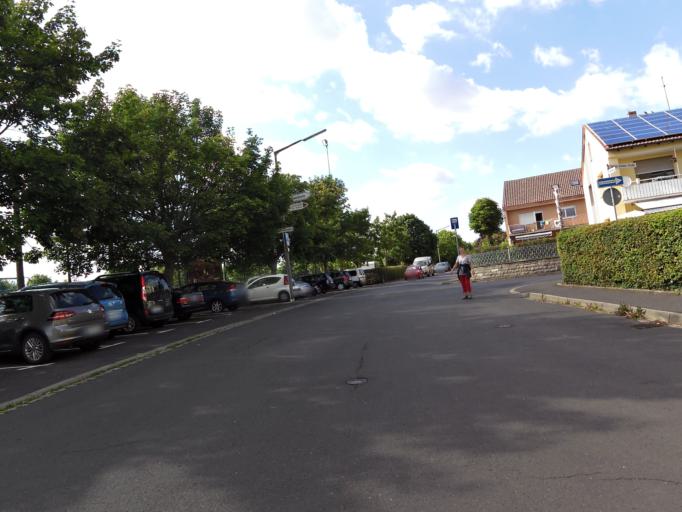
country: DE
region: Bavaria
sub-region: Regierungsbezirk Unterfranken
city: Gerbrunn
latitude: 49.7826
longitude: 9.9825
